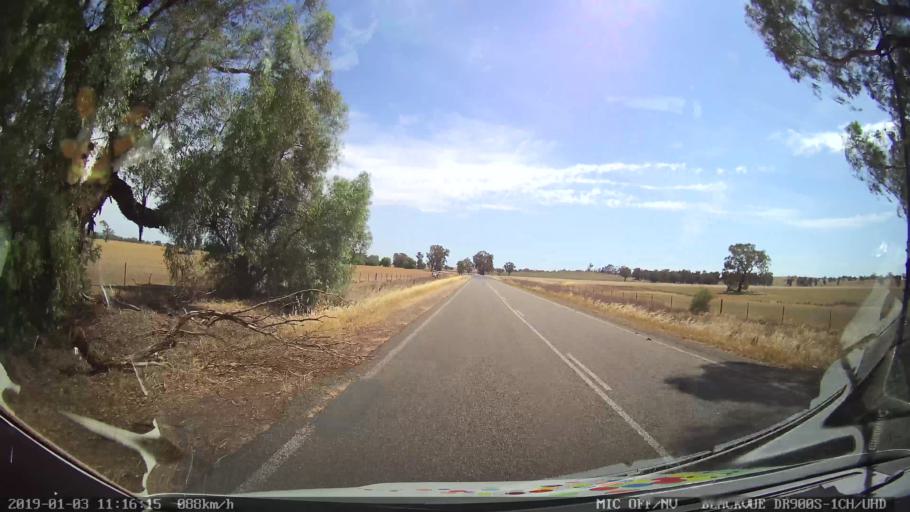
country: AU
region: New South Wales
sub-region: Young
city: Young
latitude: -34.1543
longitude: 148.2693
